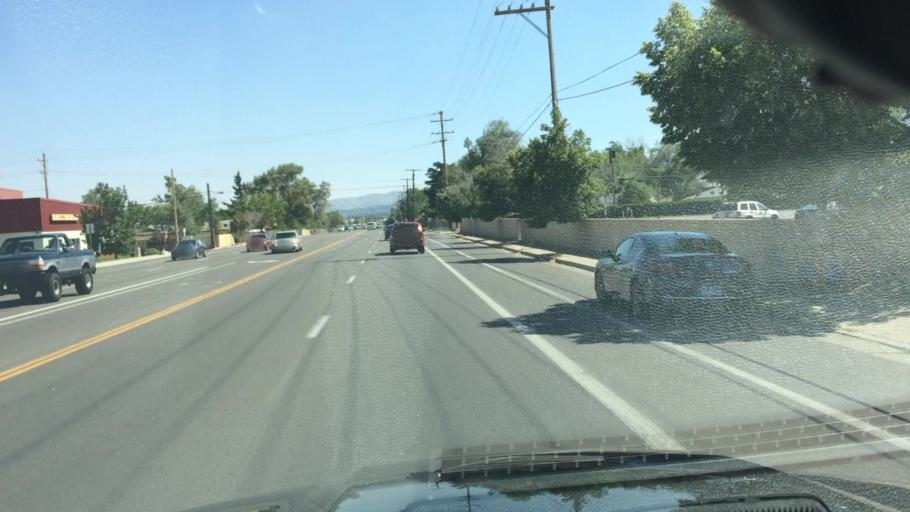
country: US
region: Nevada
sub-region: Washoe County
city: Reno
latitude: 39.5126
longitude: -119.7893
